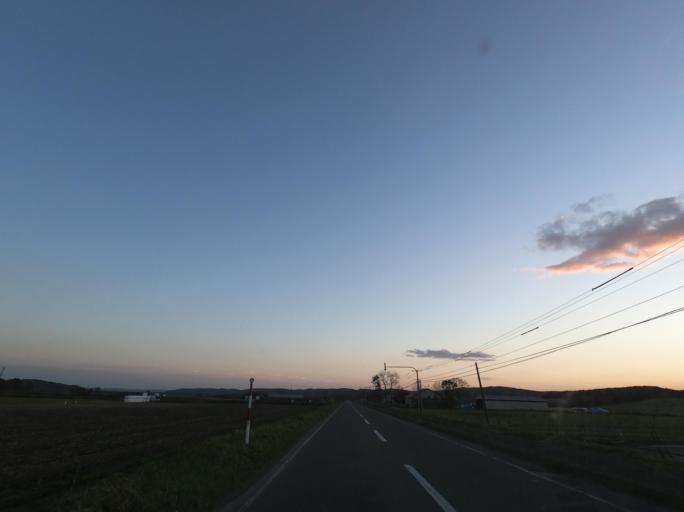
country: JP
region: Hokkaido
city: Kushiro
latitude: 43.2106
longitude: 144.4291
